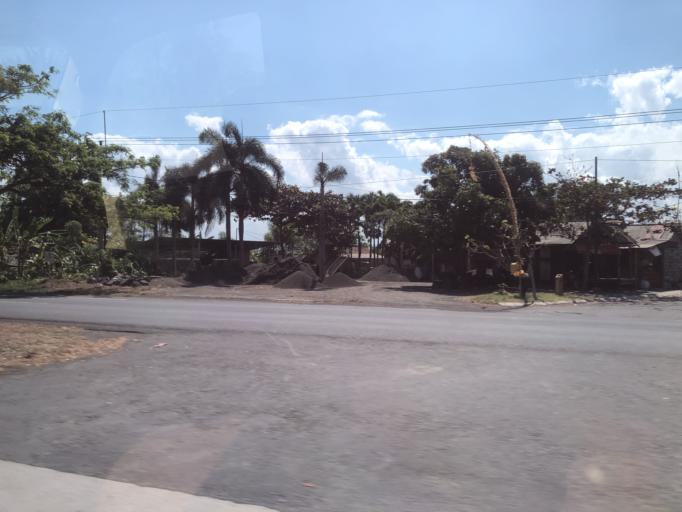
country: ID
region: Bali
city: Semarapura
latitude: -8.5683
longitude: 115.4100
